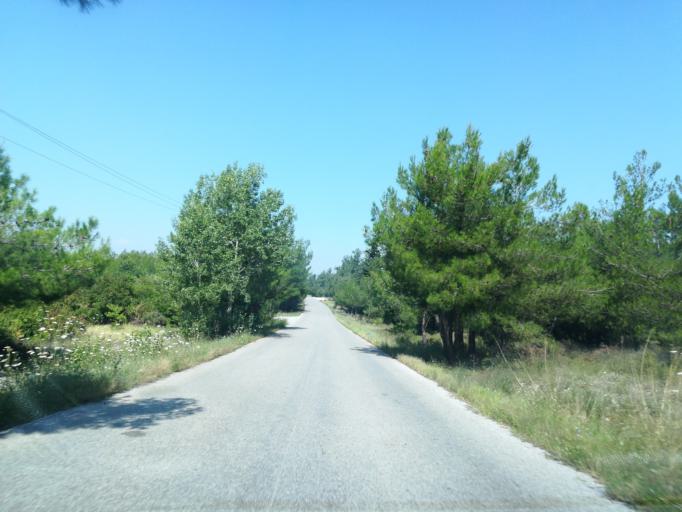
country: GR
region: Central Macedonia
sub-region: Nomos Thessalonikis
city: Pefka
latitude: 40.6464
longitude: 22.9914
